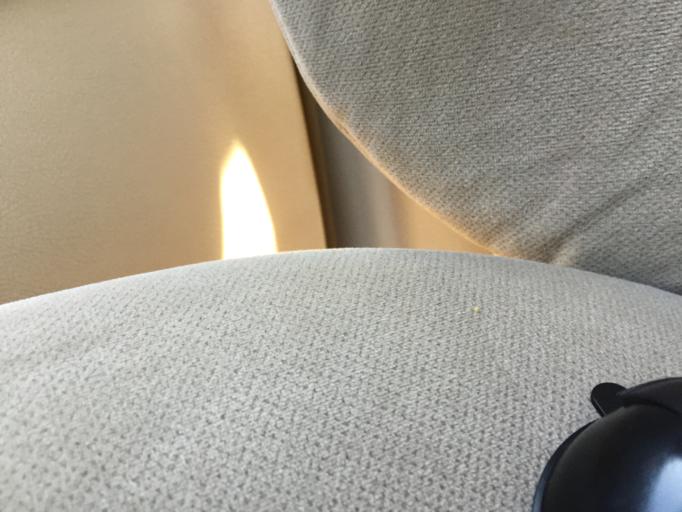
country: MX
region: Mexico City
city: Azcapotzalco
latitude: 19.4996
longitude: -99.1730
